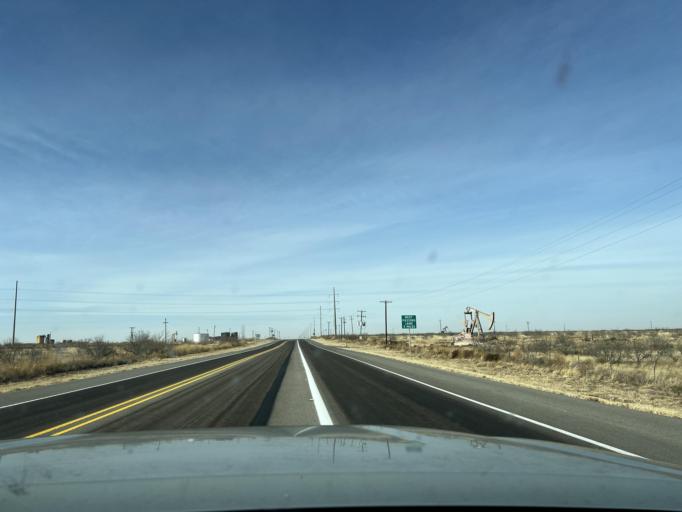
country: US
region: Texas
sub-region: Andrews County
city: Andrews
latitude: 32.3332
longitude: -102.6548
